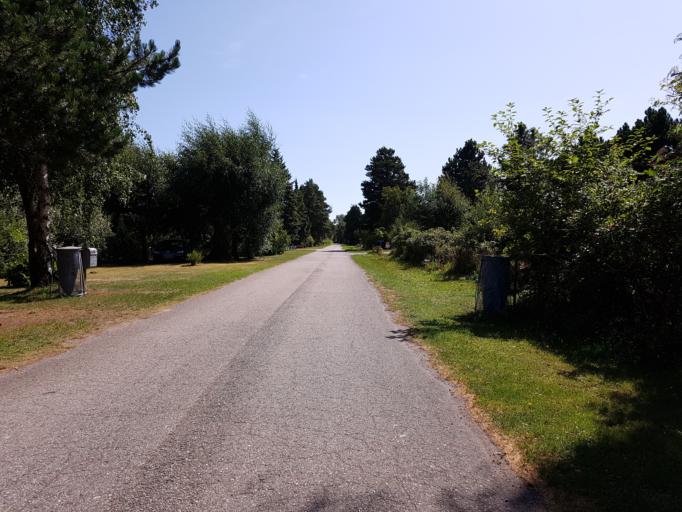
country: DK
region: Zealand
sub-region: Guldborgsund Kommune
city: Nykobing Falster
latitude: 54.5955
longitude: 11.9607
